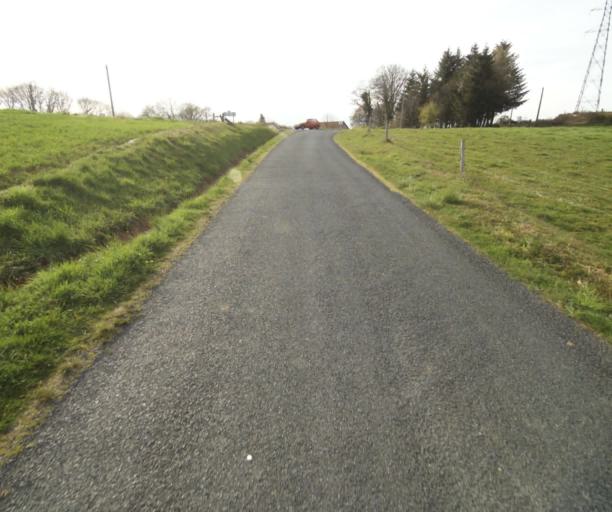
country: FR
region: Limousin
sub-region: Departement de la Correze
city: Naves
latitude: 45.3127
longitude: 1.7486
